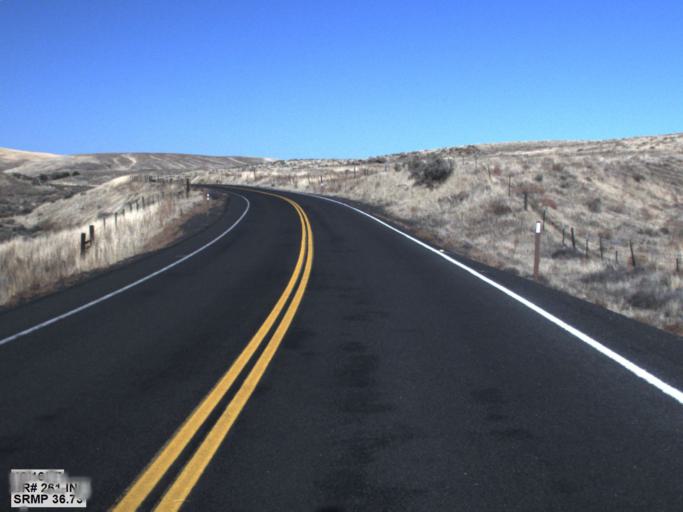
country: US
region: Washington
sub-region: Adams County
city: Ritzville
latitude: 46.7642
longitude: -118.2926
